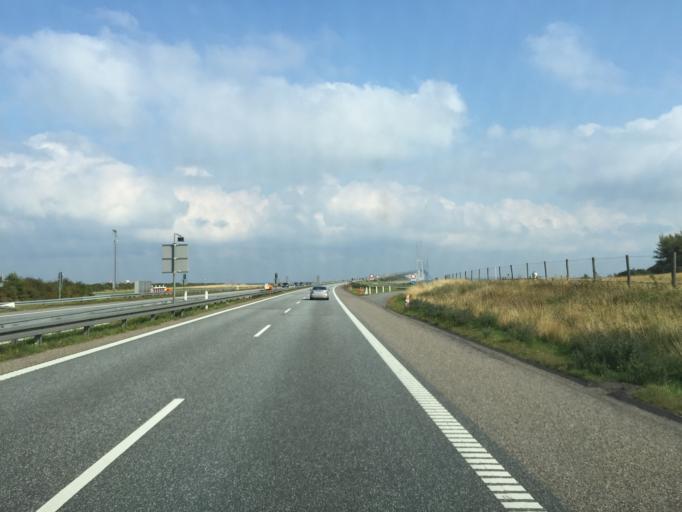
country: DK
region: Zealand
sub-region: Slagelse Kommune
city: Korsor
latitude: 55.3314
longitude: 10.9640
